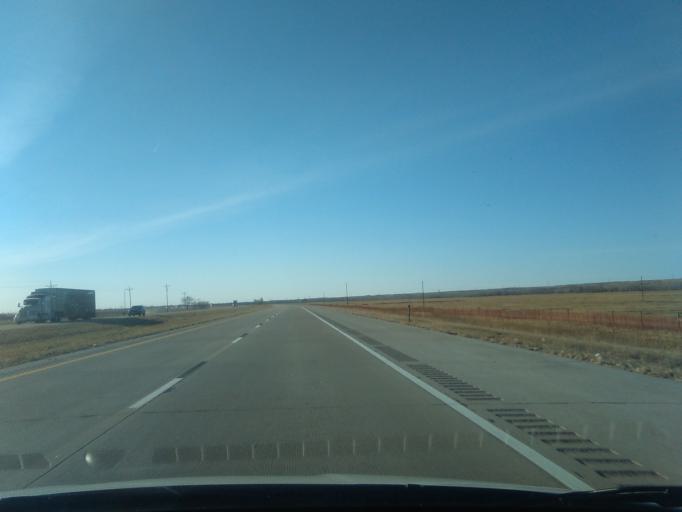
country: US
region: Colorado
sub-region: Sedgwick County
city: Julesburg
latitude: 41.0626
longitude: -102.0122
